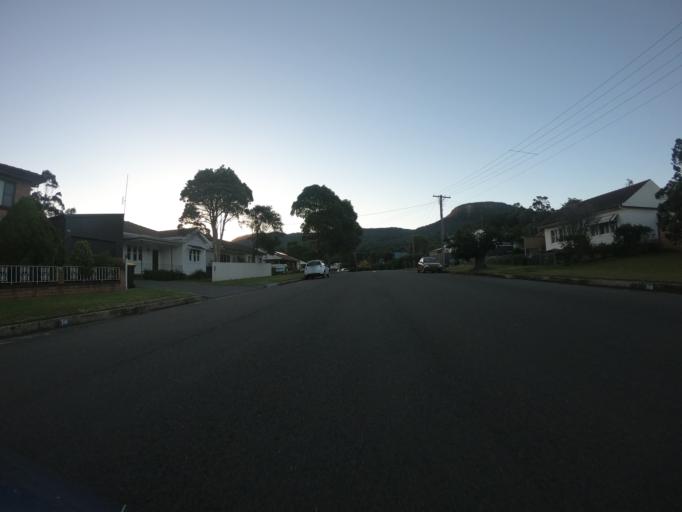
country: AU
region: New South Wales
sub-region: Wollongong
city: West Wollongong
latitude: -34.4228
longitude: 150.8600
